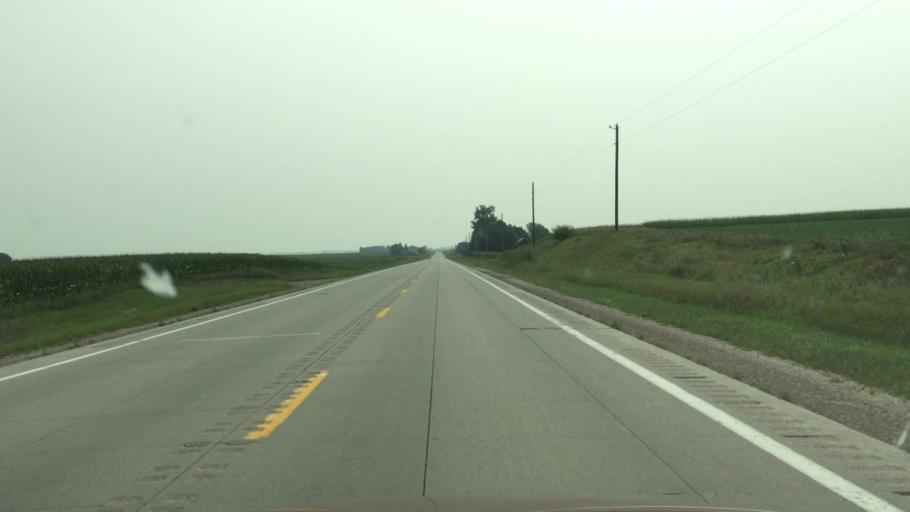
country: US
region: Iowa
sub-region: Osceola County
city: Sibley
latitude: 43.4327
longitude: -95.6545
